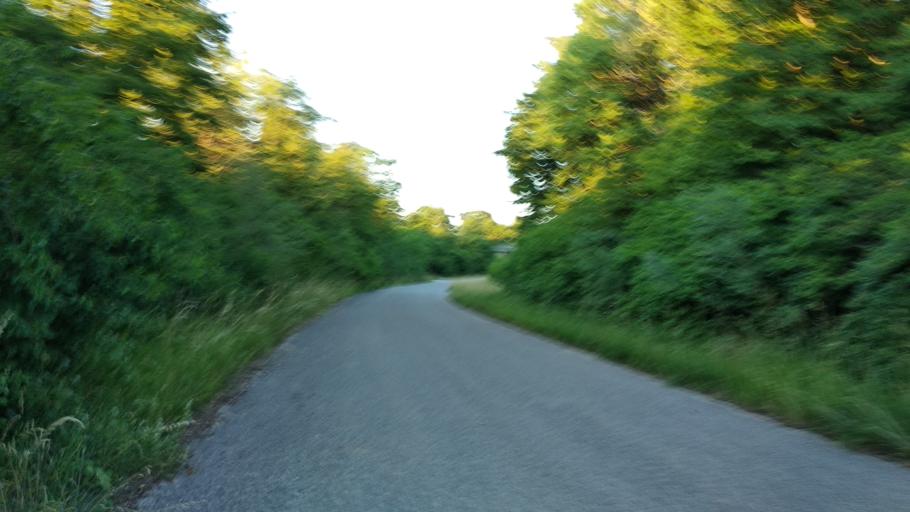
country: DE
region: Bavaria
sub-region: Upper Bavaria
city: Vaterstetten
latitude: 48.1265
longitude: 11.7570
